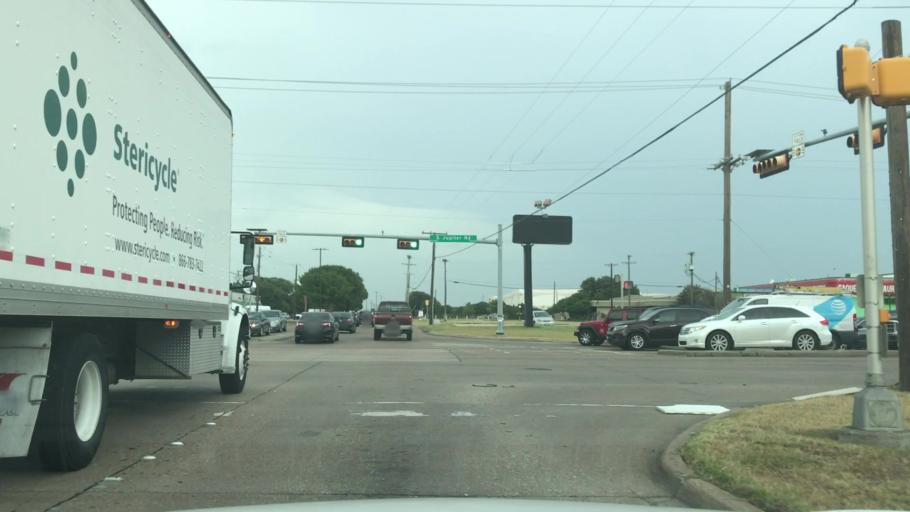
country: US
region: Texas
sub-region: Dallas County
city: Garland
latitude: 32.8788
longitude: -96.6834
